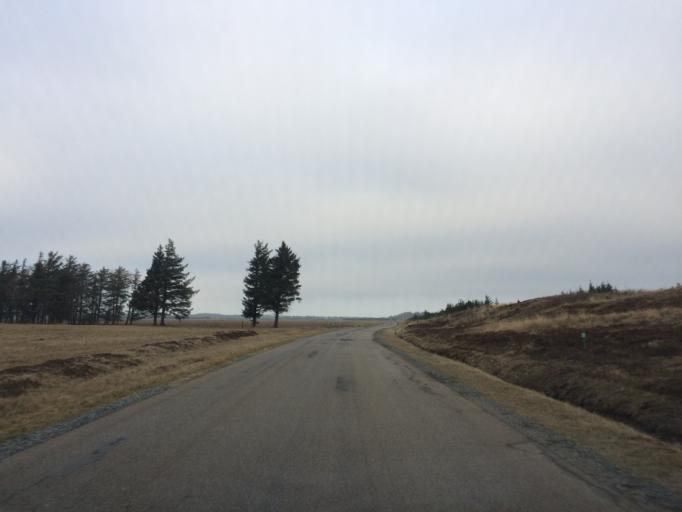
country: DK
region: South Denmark
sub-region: Varde Kommune
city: Oksbol
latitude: 55.6437
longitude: 8.1779
